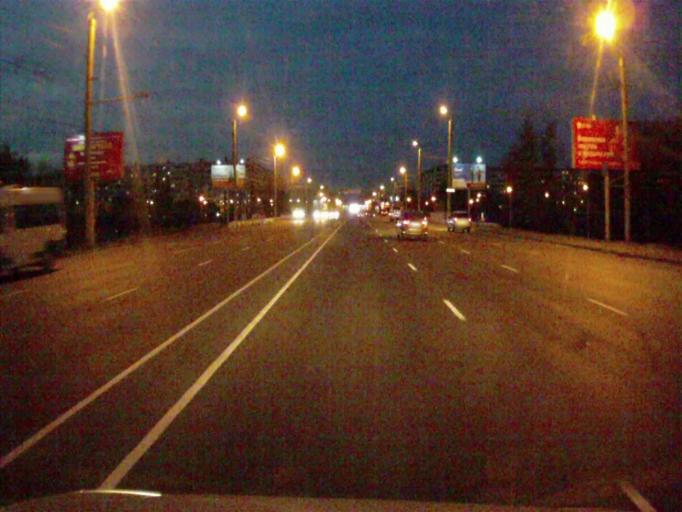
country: RU
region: Chelyabinsk
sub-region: Gorod Chelyabinsk
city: Chelyabinsk
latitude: 55.1728
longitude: 61.3582
